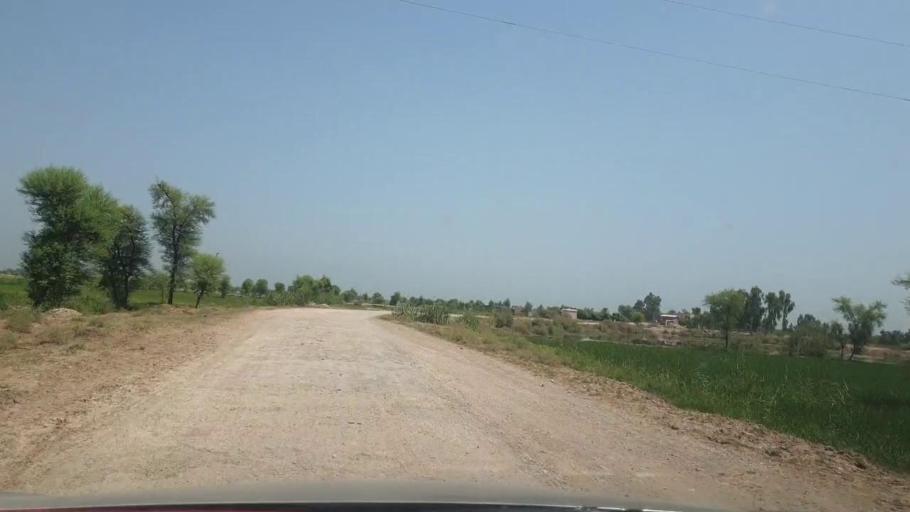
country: PK
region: Sindh
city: Warah
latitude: 27.5092
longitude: 67.7887
